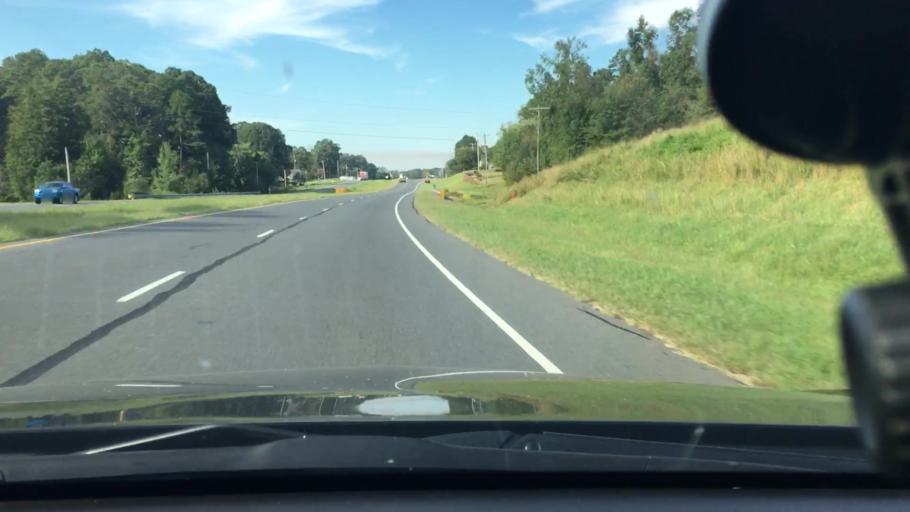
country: US
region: North Carolina
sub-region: Stanly County
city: Oakboro
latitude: 35.2755
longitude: -80.3098
